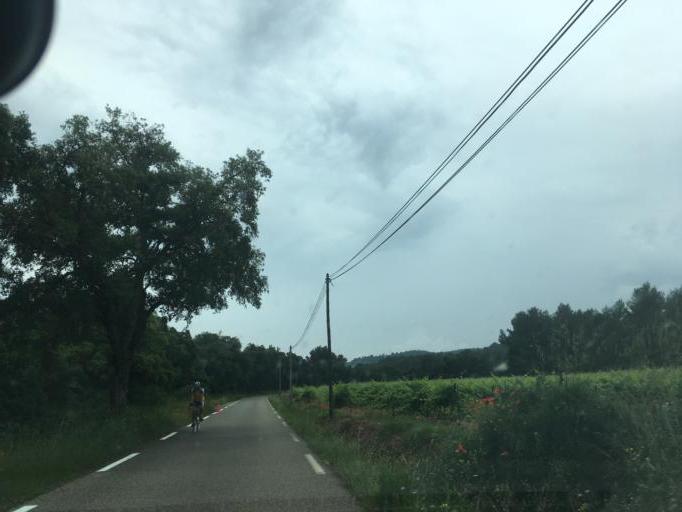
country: FR
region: Provence-Alpes-Cote d'Azur
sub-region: Departement du Var
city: La Londe-les-Maures
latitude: 43.1754
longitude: 6.2157
